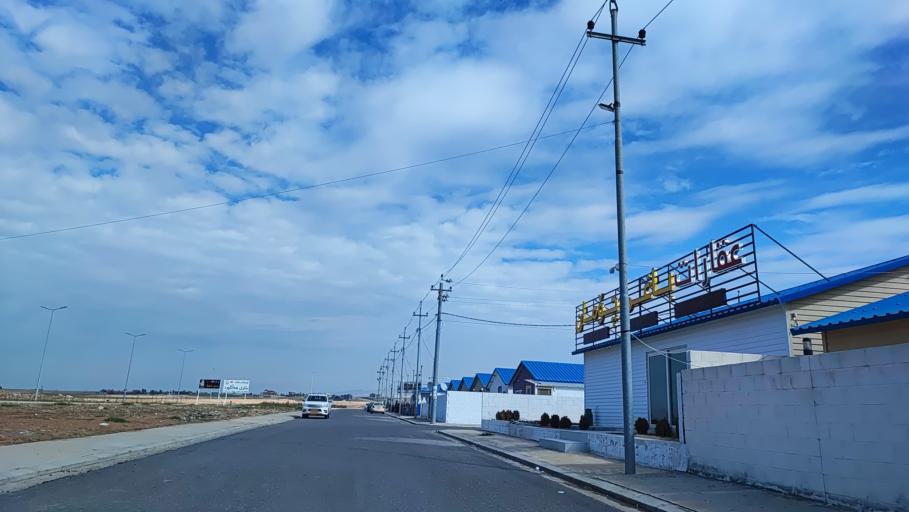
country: IQ
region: Arbil
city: Erbil
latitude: 36.2859
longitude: 44.0731
